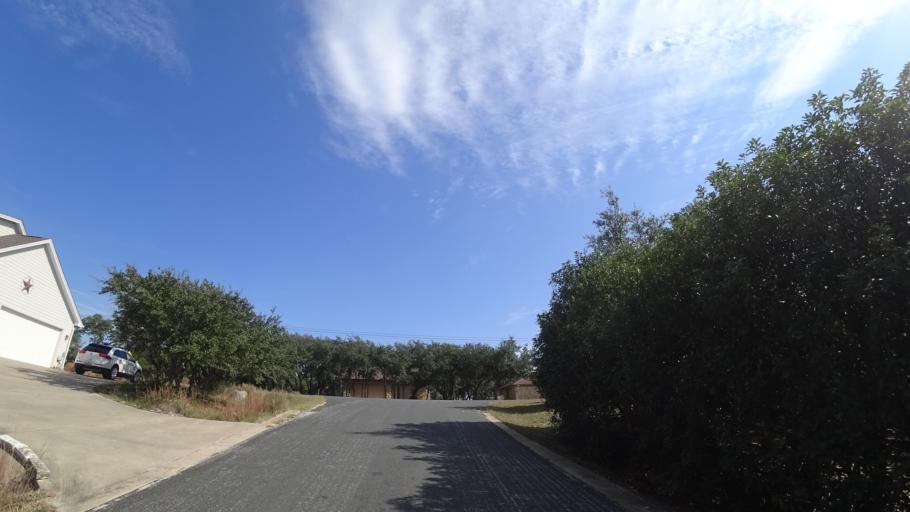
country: US
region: Texas
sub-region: Travis County
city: Bee Cave
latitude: 30.2232
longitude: -97.9364
